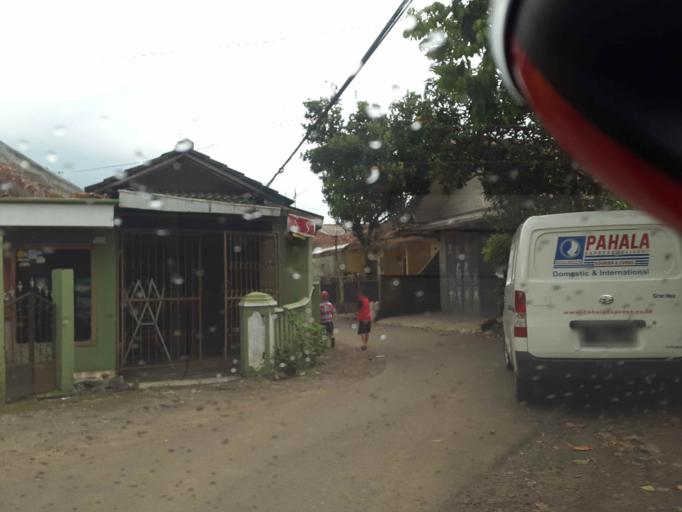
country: ID
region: West Java
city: Sukabumi
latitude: -6.9247
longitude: 106.9058
